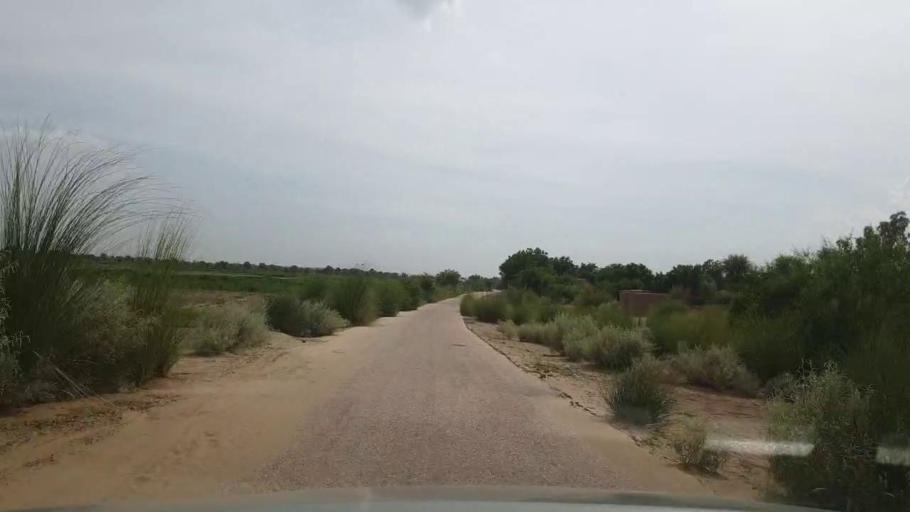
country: PK
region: Sindh
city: Kot Diji
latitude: 27.1488
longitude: 69.0312
